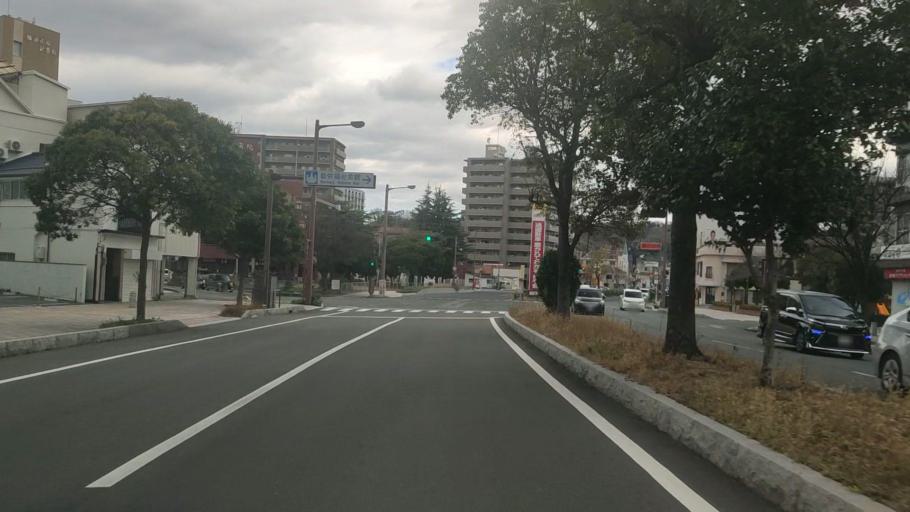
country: JP
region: Yamaguchi
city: Shimonoseki
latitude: 33.9599
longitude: 130.9418
